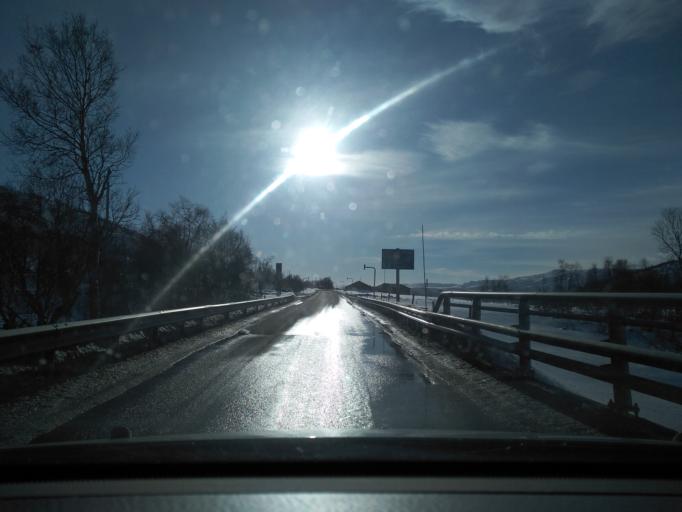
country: NO
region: Aust-Agder
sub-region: Bykle
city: Hovden
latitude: 59.6453
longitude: 7.4618
